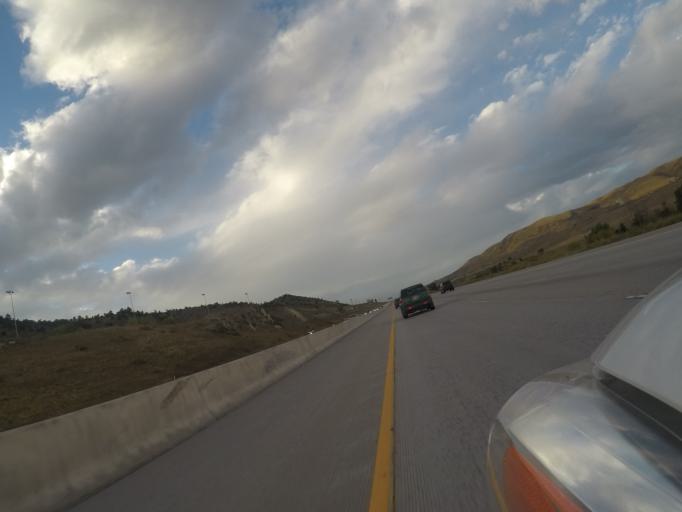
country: US
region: Colorado
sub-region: Jefferson County
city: West Pleasant View
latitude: 39.6677
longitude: -105.1869
